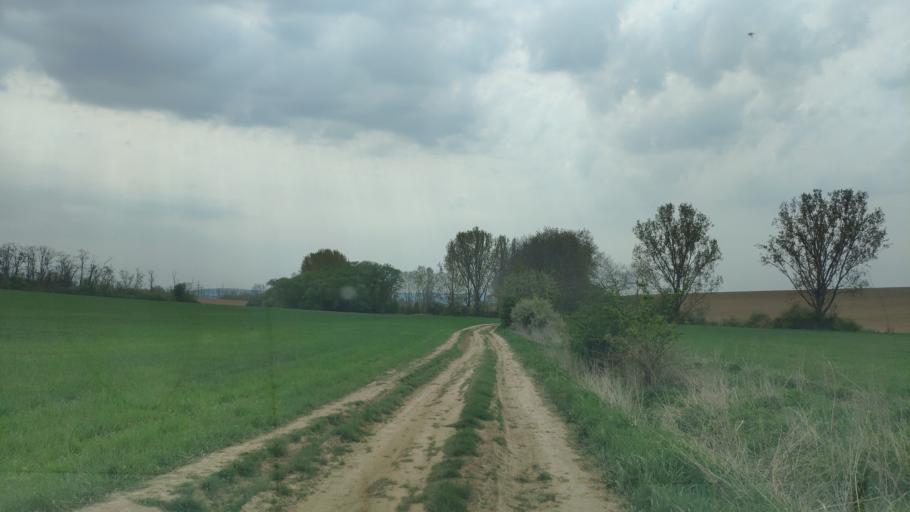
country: SK
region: Kosicky
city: Moldava nad Bodvou
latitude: 48.6142
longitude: 21.0390
